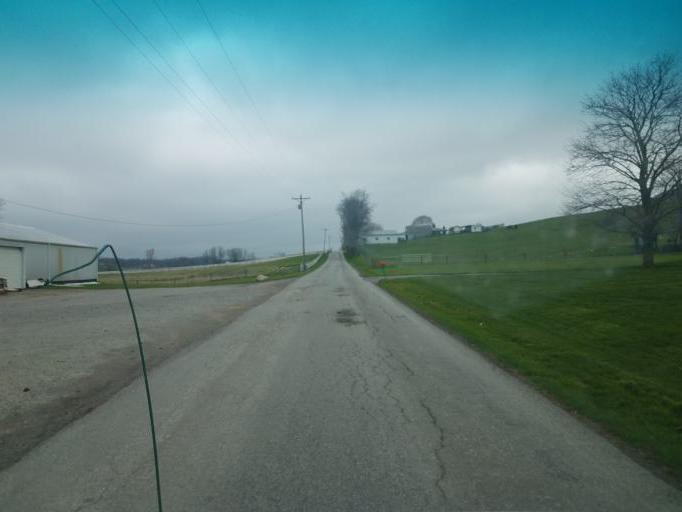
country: US
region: Ohio
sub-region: Tuscarawas County
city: Sugarcreek
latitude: 40.6063
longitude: -81.7317
